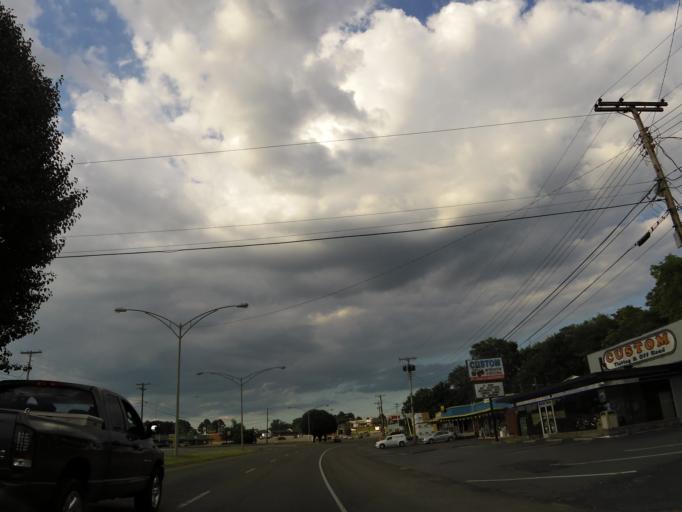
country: US
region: Tennessee
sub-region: Maury County
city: Columbia
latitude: 35.6244
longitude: -87.0327
